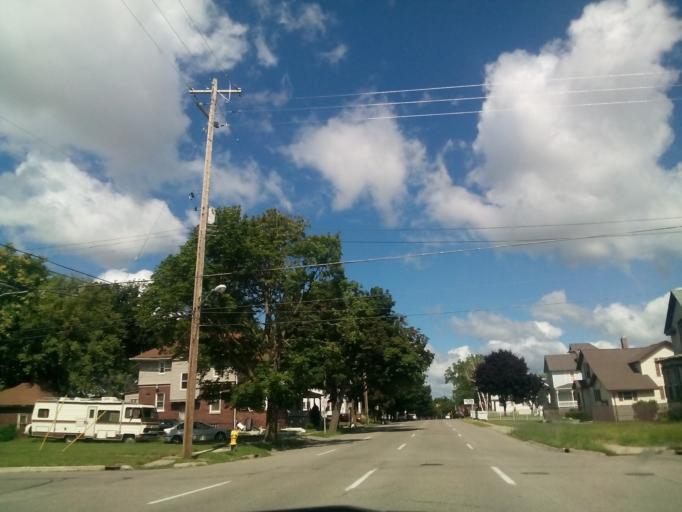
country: US
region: Michigan
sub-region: Genesee County
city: Flint
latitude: 43.0083
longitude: -83.6872
